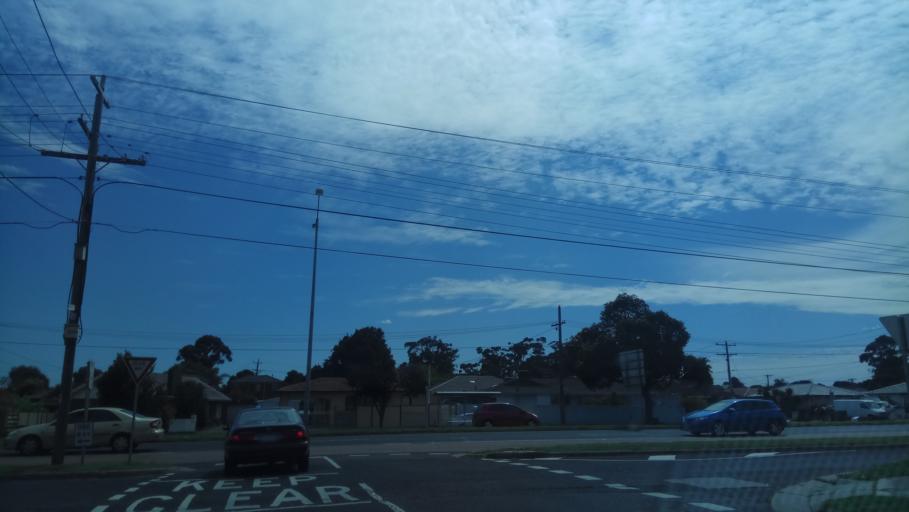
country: AU
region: Victoria
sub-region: Greater Dandenong
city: Springvale South
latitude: -37.9656
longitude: 145.1500
